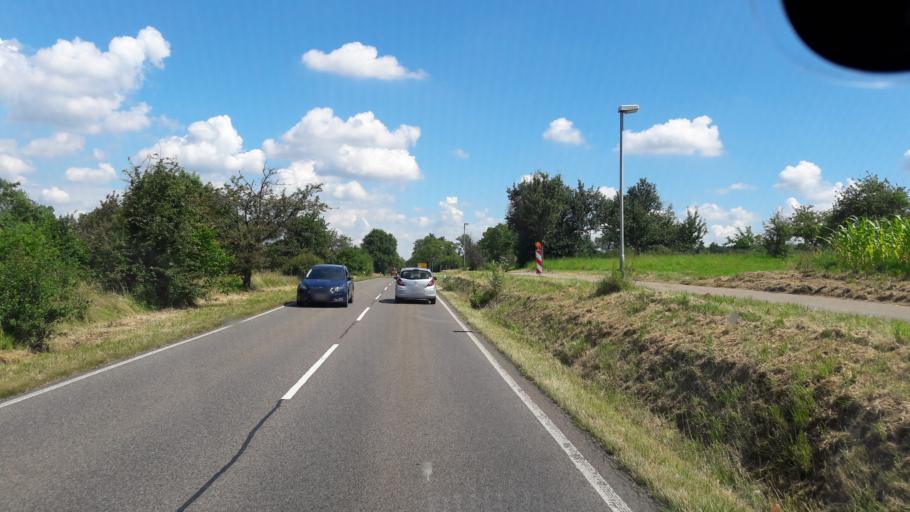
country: DE
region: Baden-Wuerttemberg
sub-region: Karlsruhe Region
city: Ettlingen
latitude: 48.9183
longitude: 8.3797
